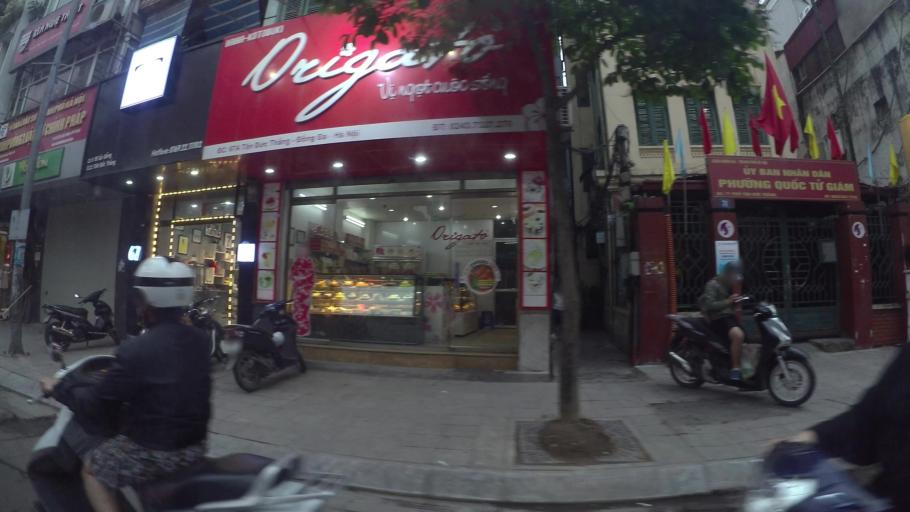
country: VN
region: Ha Noi
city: Dong Da
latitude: 21.0258
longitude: 105.8333
